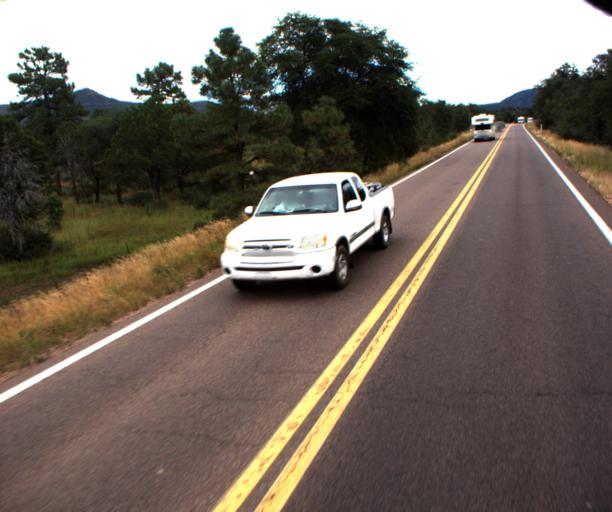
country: US
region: Arizona
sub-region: Gila County
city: Star Valley
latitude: 34.2644
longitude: -111.2279
